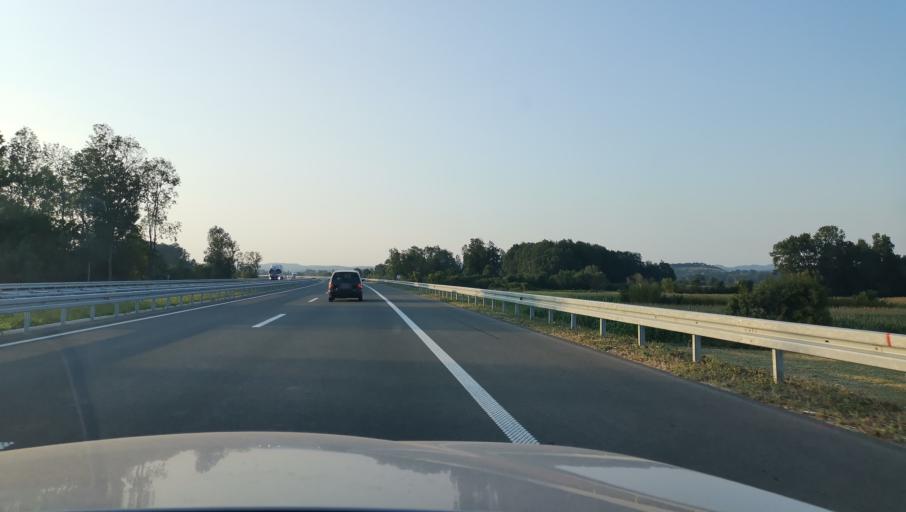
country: RS
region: Central Serbia
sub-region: Kolubarski Okrug
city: Ljig
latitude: 44.2683
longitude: 20.2695
